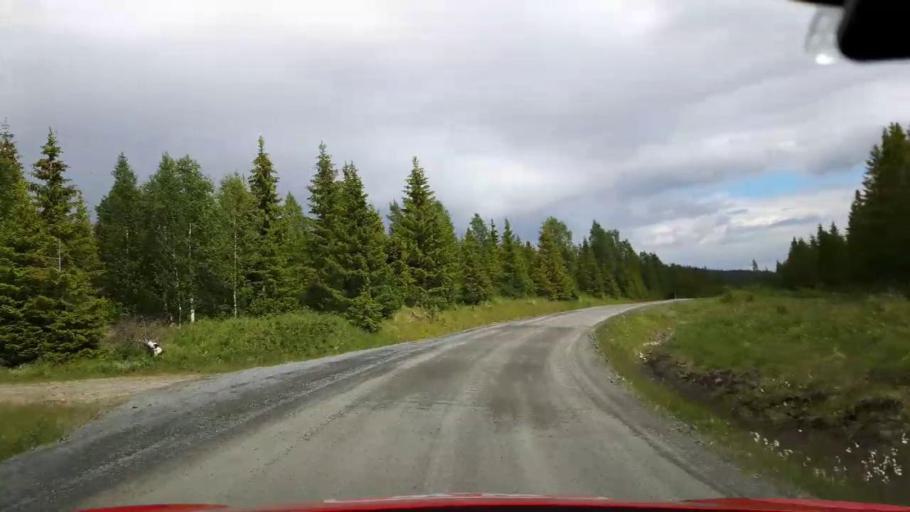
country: NO
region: Nord-Trondelag
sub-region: Lierne
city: Sandvika
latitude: 64.1448
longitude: 13.9206
